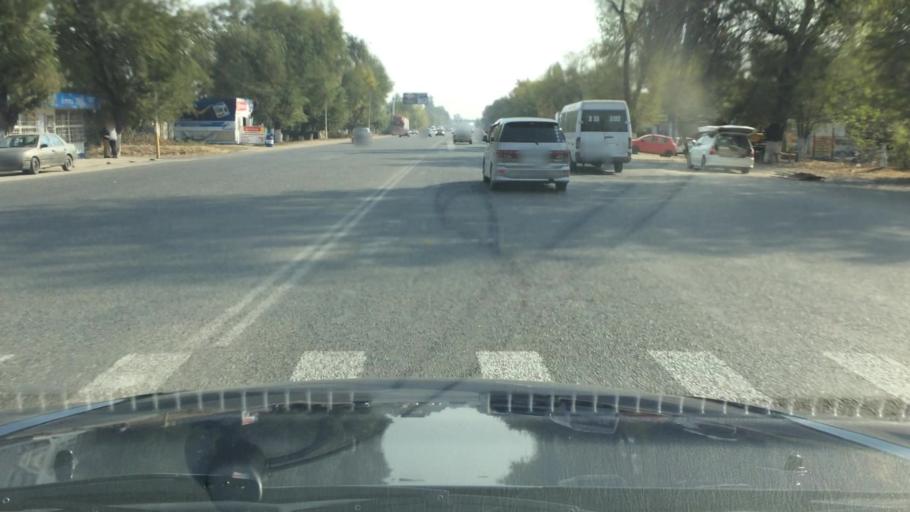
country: KG
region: Chuy
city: Lebedinovka
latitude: 42.8868
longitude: 74.6725
